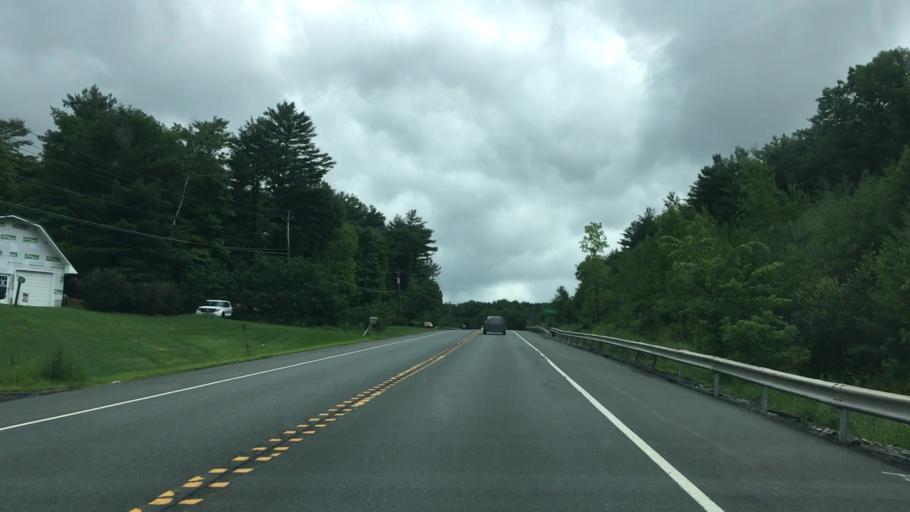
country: US
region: New York
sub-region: Rensselaer County
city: Hoosick Falls
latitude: 42.8472
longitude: -73.3985
